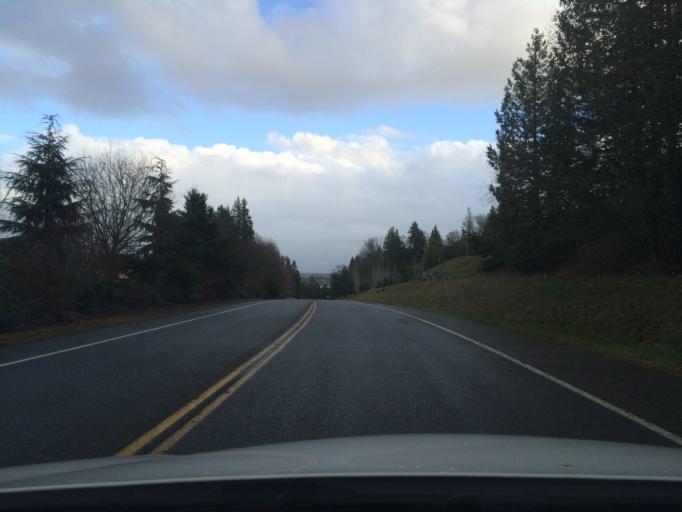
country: US
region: Washington
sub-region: Whatcom County
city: Blaine
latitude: 48.9655
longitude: -122.7798
